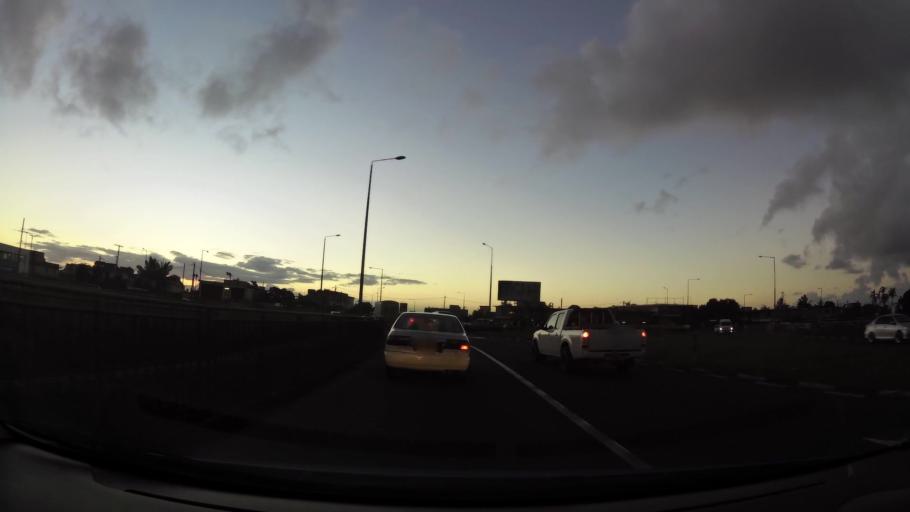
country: MU
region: Plaines Wilhems
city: Curepipe
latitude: -20.2875
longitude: 57.5251
